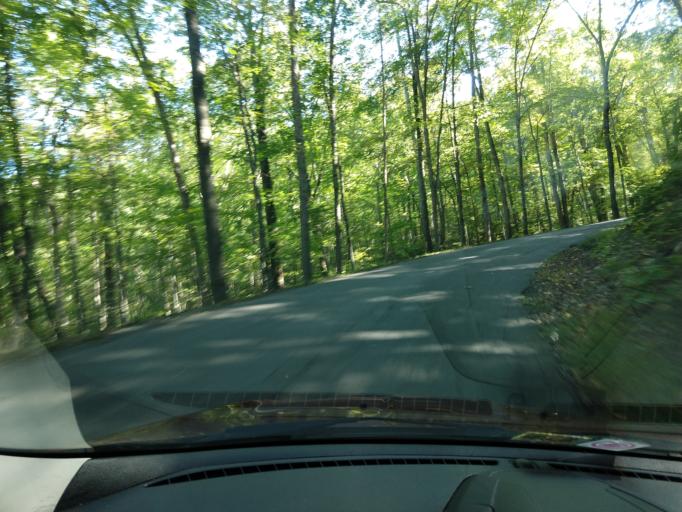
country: US
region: Virginia
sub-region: Alleghany County
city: Clifton Forge
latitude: 37.8504
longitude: -79.8514
